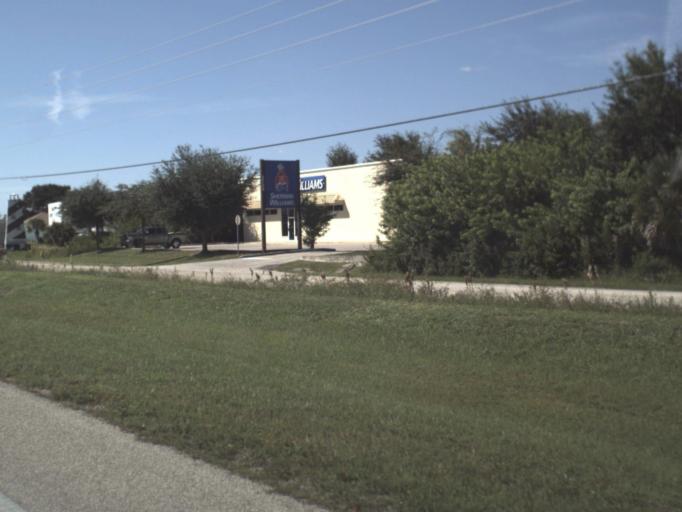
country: US
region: Florida
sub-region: Charlotte County
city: Grove City
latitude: 26.9329
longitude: -82.2842
